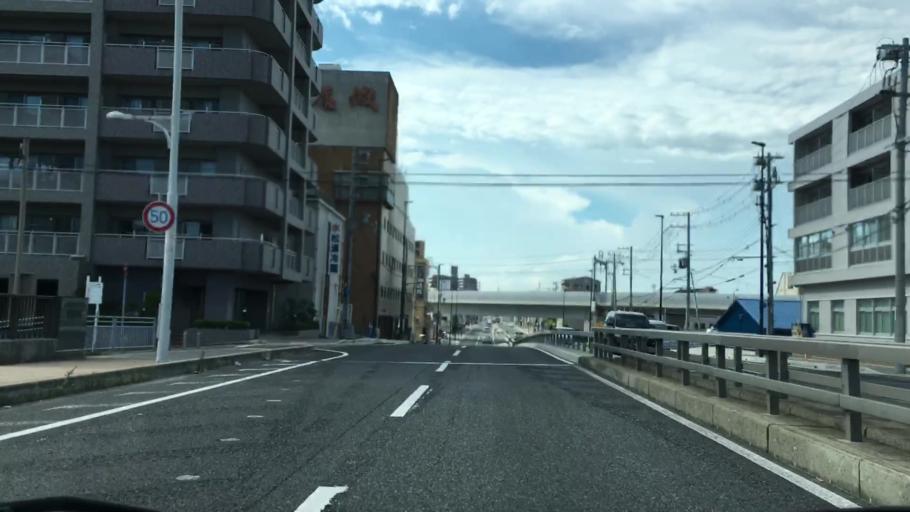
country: JP
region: Hyogo
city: Akashi
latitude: 34.6488
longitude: 134.9837
